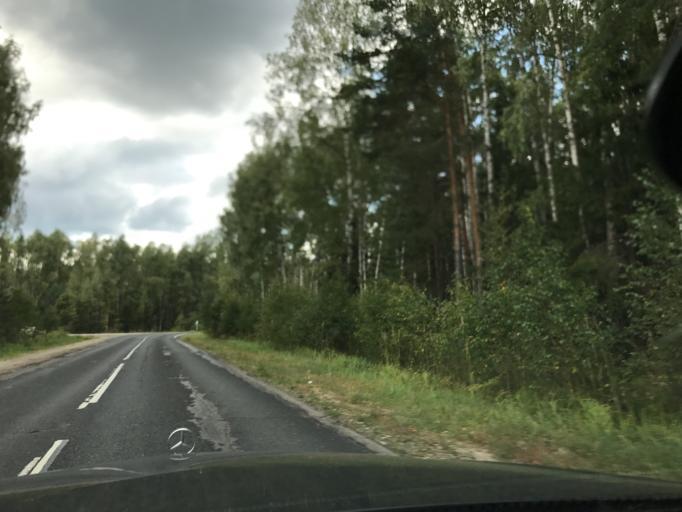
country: RU
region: Vladimir
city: Raduzhnyy
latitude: 55.9830
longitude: 40.2442
